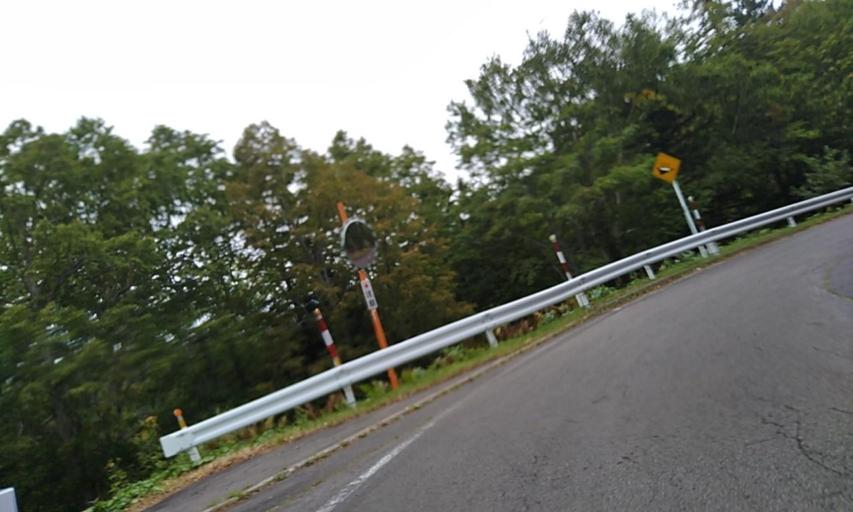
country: JP
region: Hokkaido
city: Bihoro
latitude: 43.5700
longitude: 144.1985
